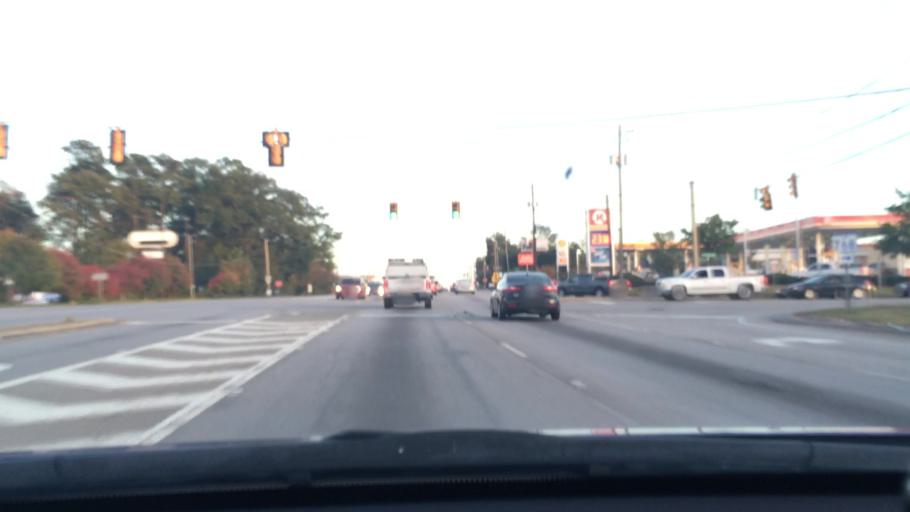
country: US
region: South Carolina
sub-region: Richland County
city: Hopkins
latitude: 33.9550
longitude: -80.9257
